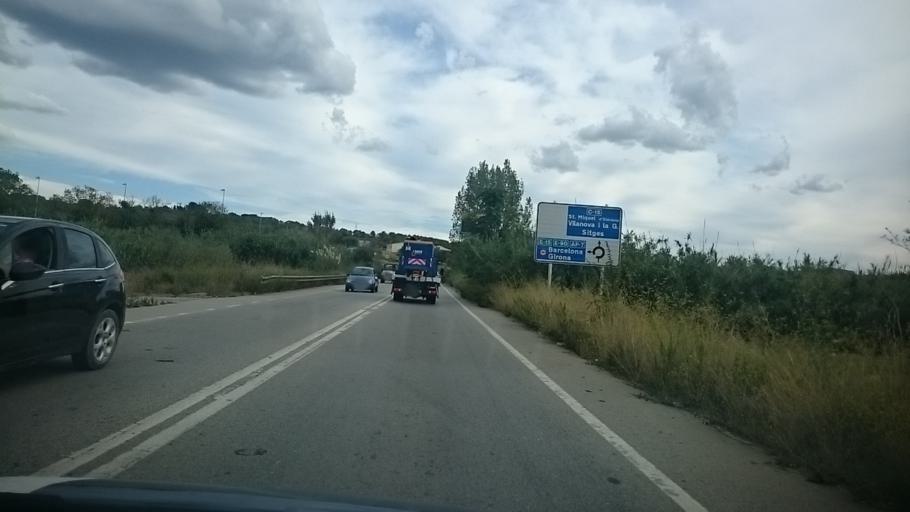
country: ES
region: Catalonia
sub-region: Provincia de Barcelona
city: Vilafranca del Penedes
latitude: 41.3345
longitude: 1.7079
